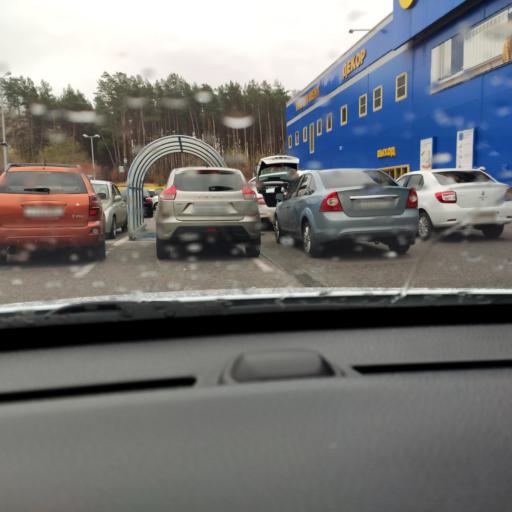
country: RU
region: Voronezj
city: Pridonskoy
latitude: 51.6464
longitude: 39.1135
